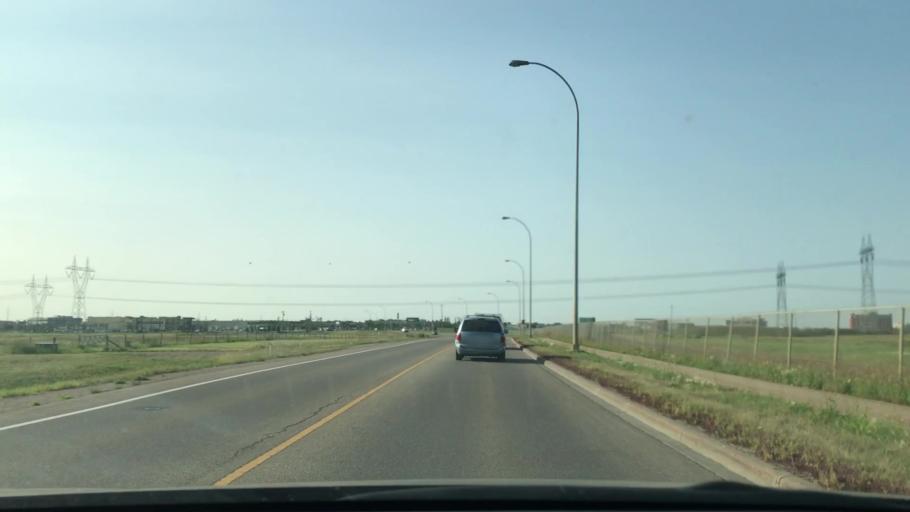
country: CA
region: Alberta
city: Beaumont
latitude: 53.4364
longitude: -113.4830
